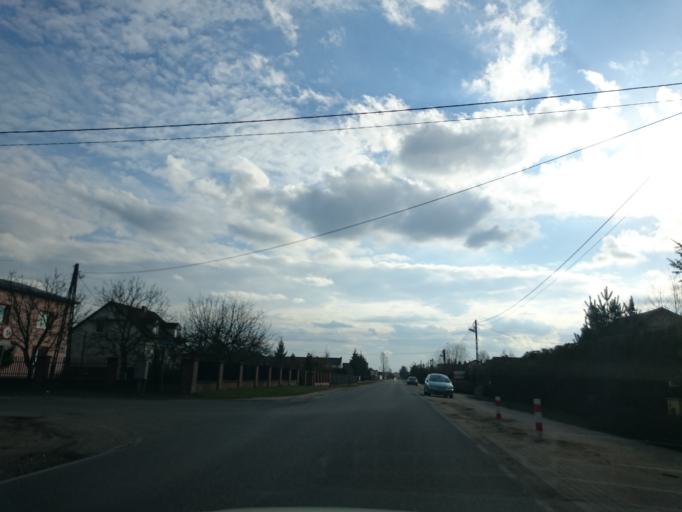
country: PL
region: Kujawsko-Pomorskie
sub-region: Powiat torunski
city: Lubicz Gorny
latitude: 53.0333
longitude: 18.7780
